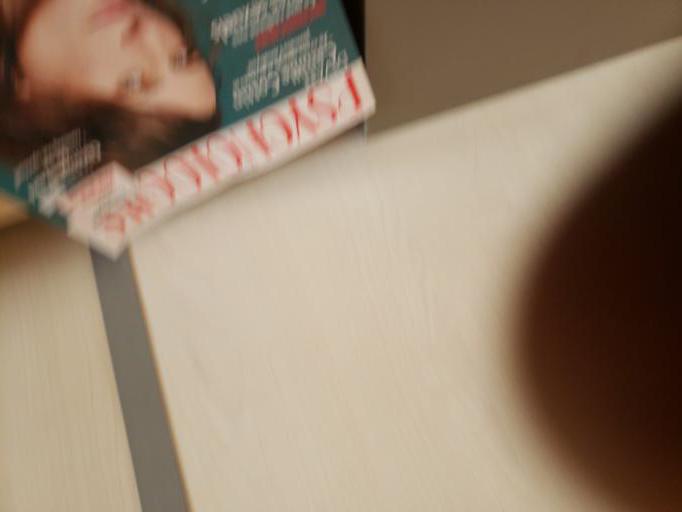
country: ML
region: Bamako
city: Bamako
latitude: 12.6314
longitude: -8.0233
